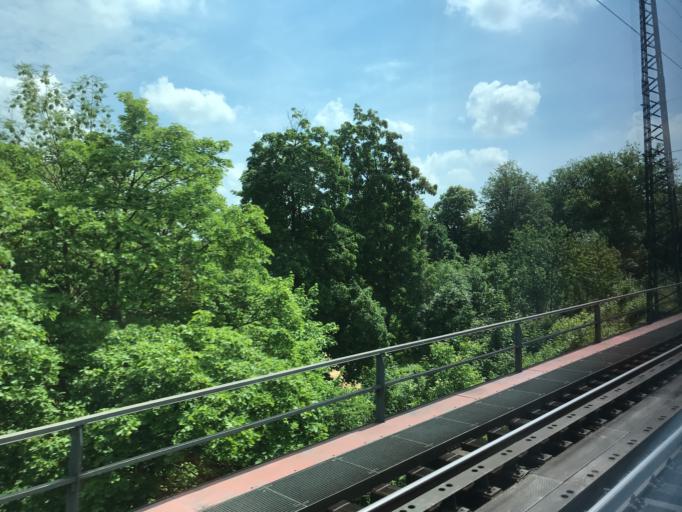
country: DE
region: Bavaria
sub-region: Swabia
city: Augsburg
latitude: 48.3749
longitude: 10.8774
